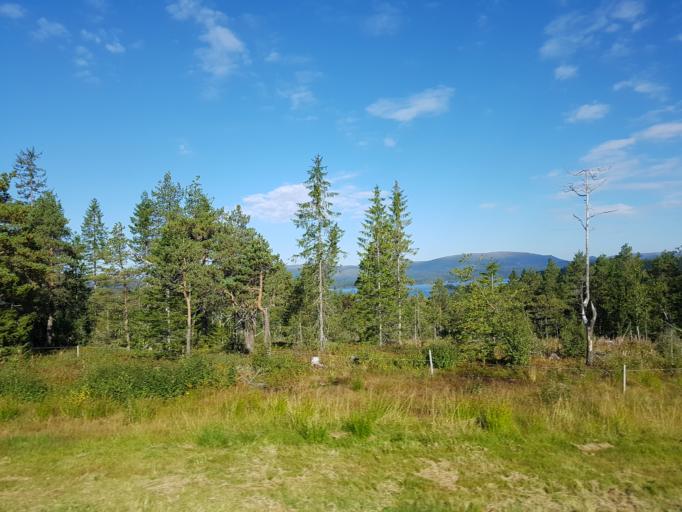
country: NO
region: Sor-Trondelag
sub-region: Trondheim
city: Trondheim
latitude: 63.5943
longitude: 10.2127
